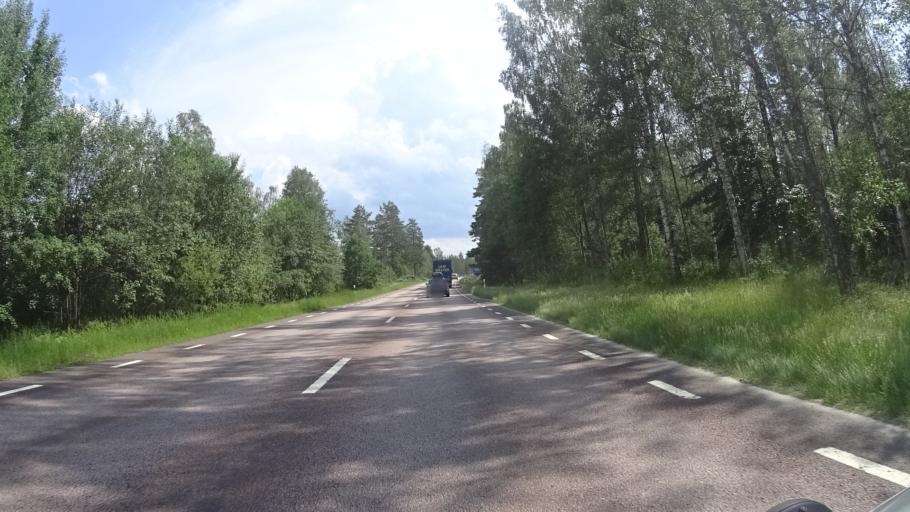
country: SE
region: Kalmar
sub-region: Hultsfreds Kommun
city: Hultsfred
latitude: 57.4760
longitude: 15.8377
